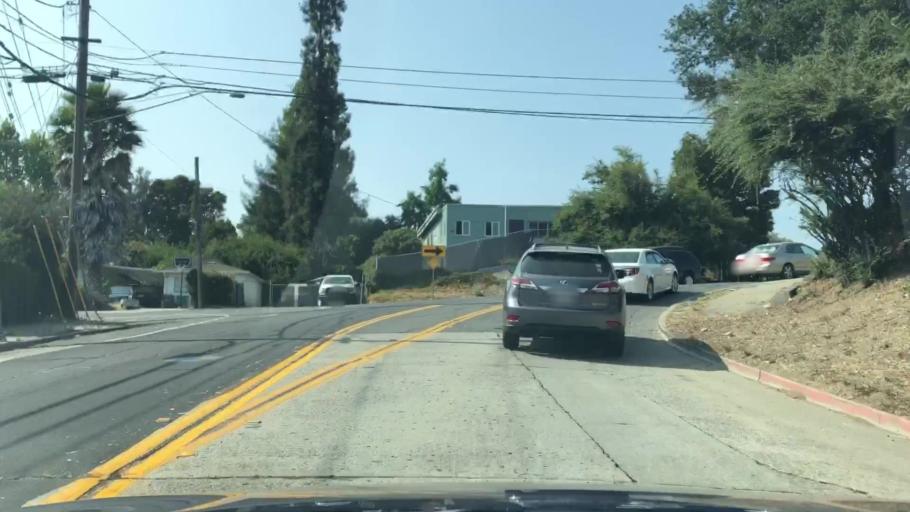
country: US
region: California
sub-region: Alameda County
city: San Leandro
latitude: 37.7739
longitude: -122.1696
